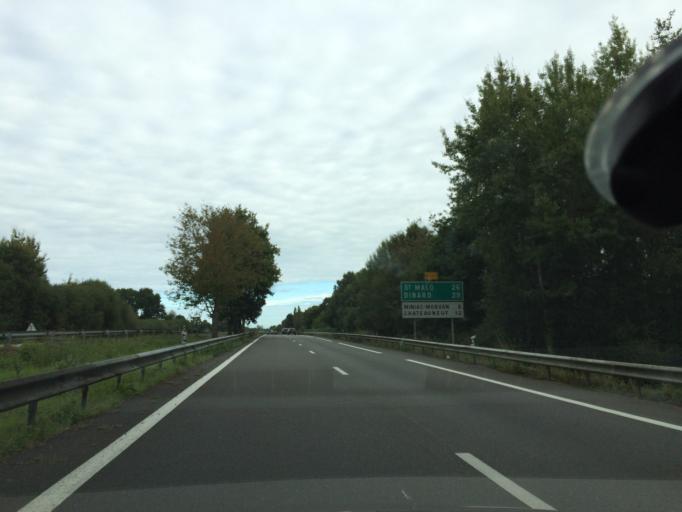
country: FR
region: Brittany
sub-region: Departement d'Ille-et-Vilaine
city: Saint-Pierre-de-Plesguen
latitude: 48.4740
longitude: -1.9111
